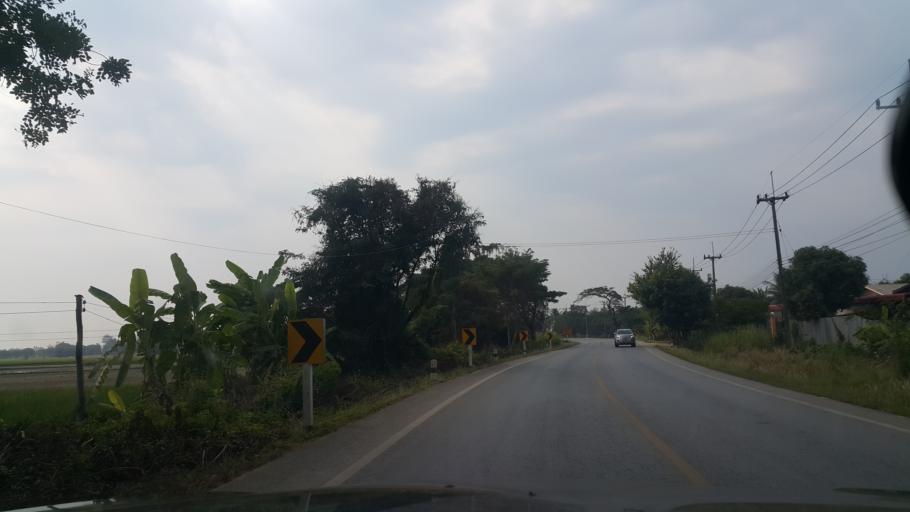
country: TH
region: Sukhothai
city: Si Samrong
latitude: 17.0953
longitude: 99.8842
